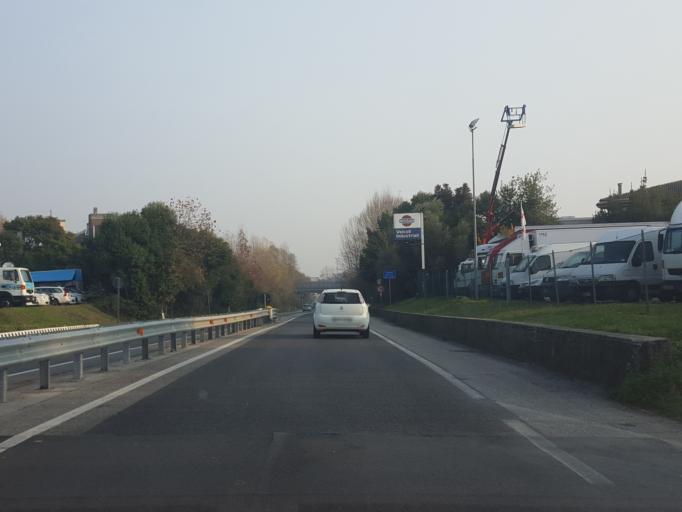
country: IT
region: Veneto
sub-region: Provincia di Treviso
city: Silea
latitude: 45.6533
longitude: 12.2913
